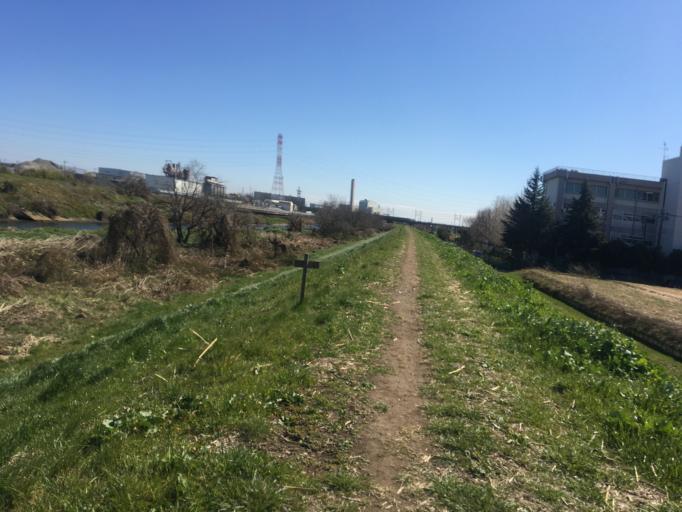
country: JP
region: Saitama
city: Shiki
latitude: 35.8259
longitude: 139.5964
